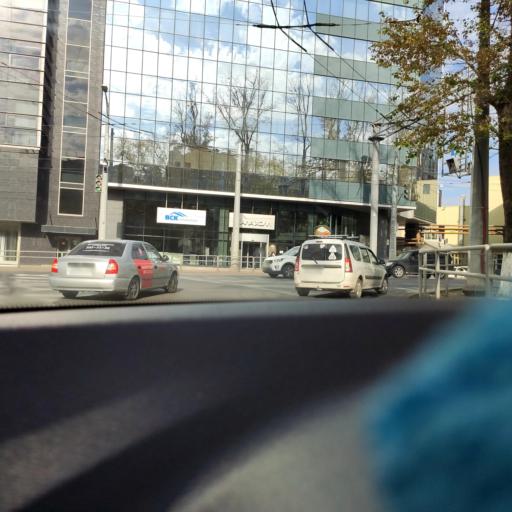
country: RU
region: Samara
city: Samara
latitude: 53.2029
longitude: 50.1450
